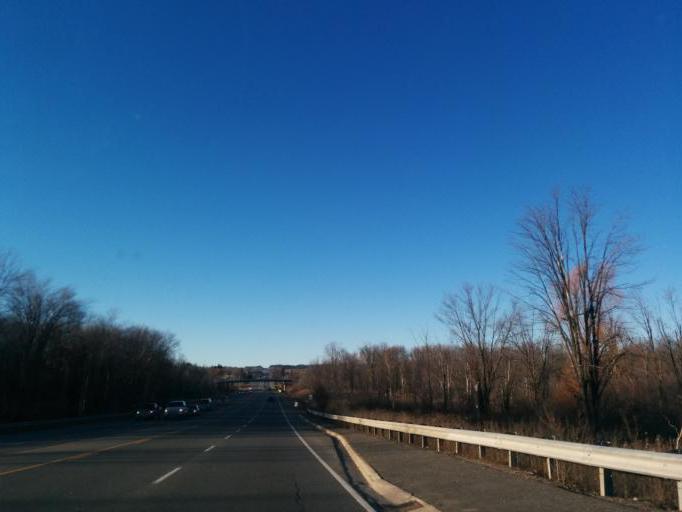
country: CA
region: Ontario
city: Orangeville
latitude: 43.8094
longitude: -79.9271
